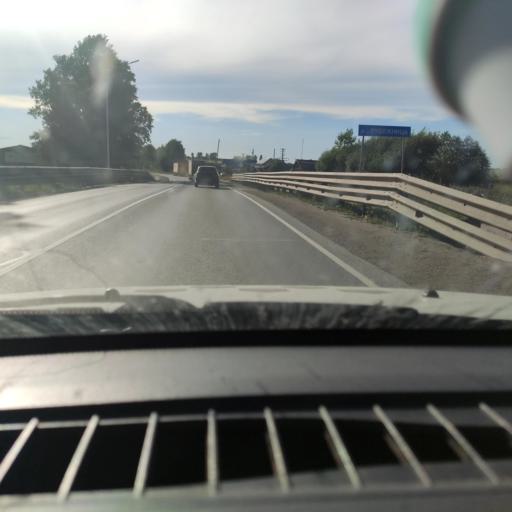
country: RU
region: Kirov
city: Vakhrushi
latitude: 58.6770
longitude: 50.0041
